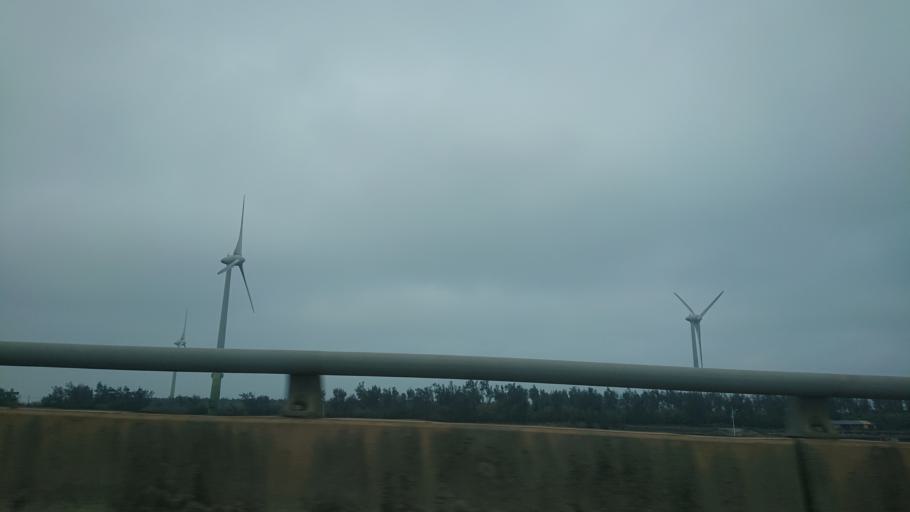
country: TW
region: Taiwan
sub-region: Miaoli
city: Miaoli
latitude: 24.4994
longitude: 120.6775
